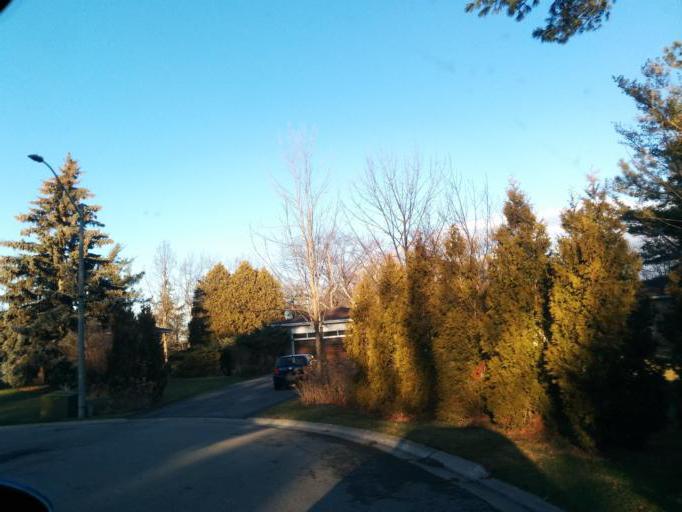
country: CA
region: Ontario
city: Mississauga
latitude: 43.5592
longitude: -79.6183
